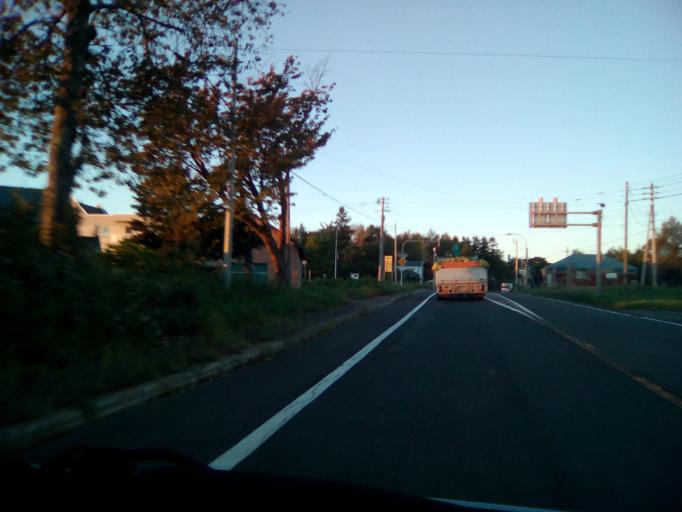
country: JP
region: Hokkaido
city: Niseko Town
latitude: 42.6938
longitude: 140.8393
